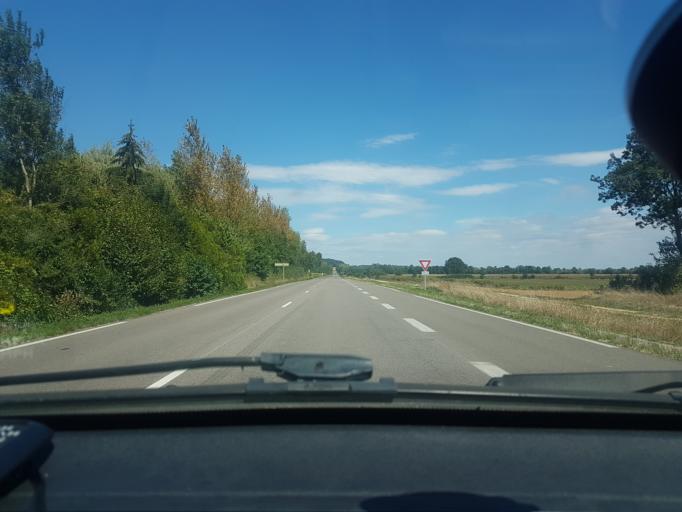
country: FR
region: Franche-Comte
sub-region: Departement de la Haute-Saone
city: Gray-la-Ville
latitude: 47.4320
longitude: 5.5378
